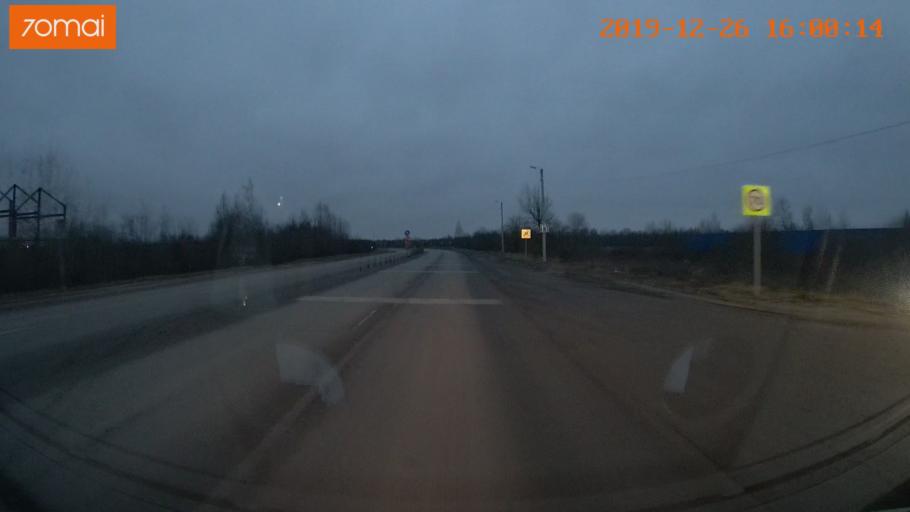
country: RU
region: Jaroslavl
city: Rybinsk
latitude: 58.0264
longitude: 38.8035
